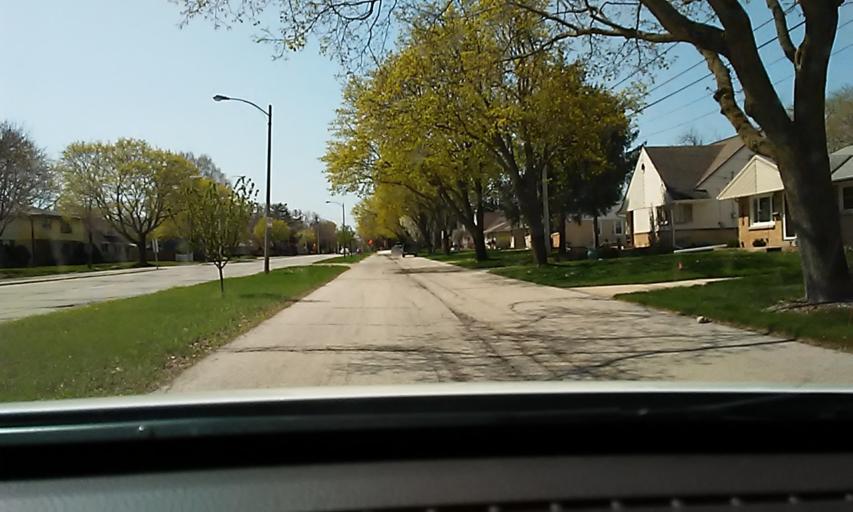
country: US
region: Wisconsin
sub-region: Milwaukee County
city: Greenfield
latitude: 42.9762
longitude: -87.9981
